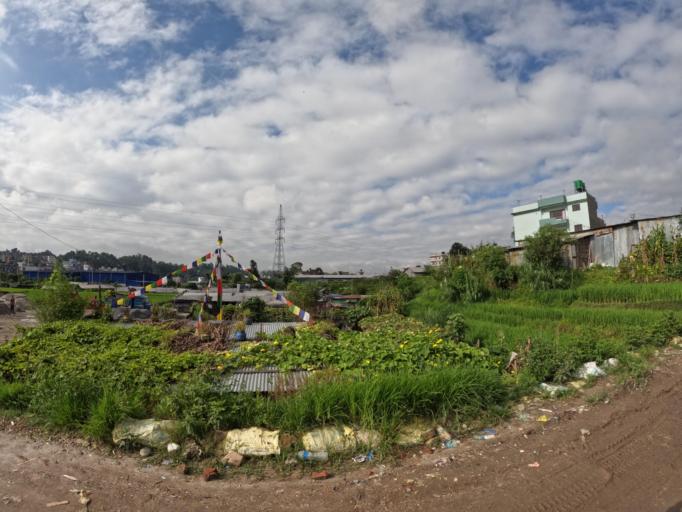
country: NP
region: Central Region
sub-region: Bagmati Zone
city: Kathmandu
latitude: 27.7645
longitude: 85.3372
